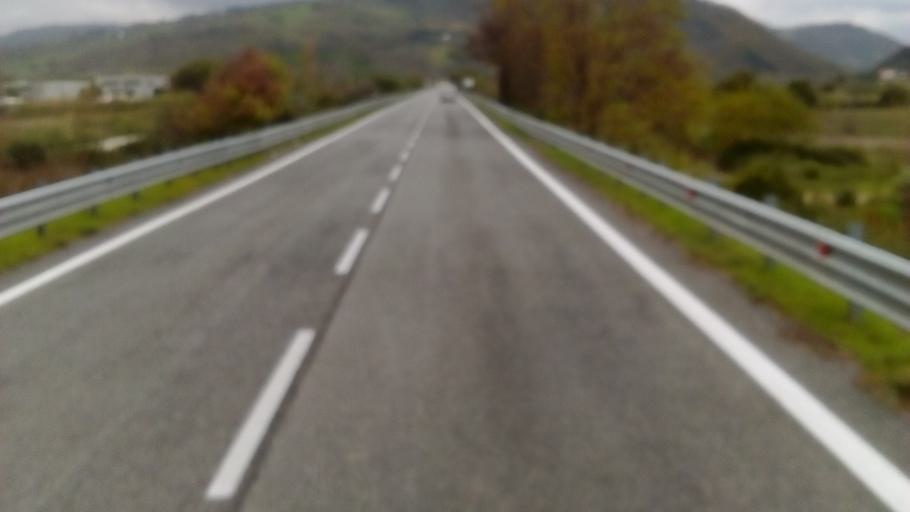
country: IT
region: Abruzzo
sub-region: Provincia di Chieti
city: San Giovanni Lipioni
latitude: 41.8064
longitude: 14.5660
